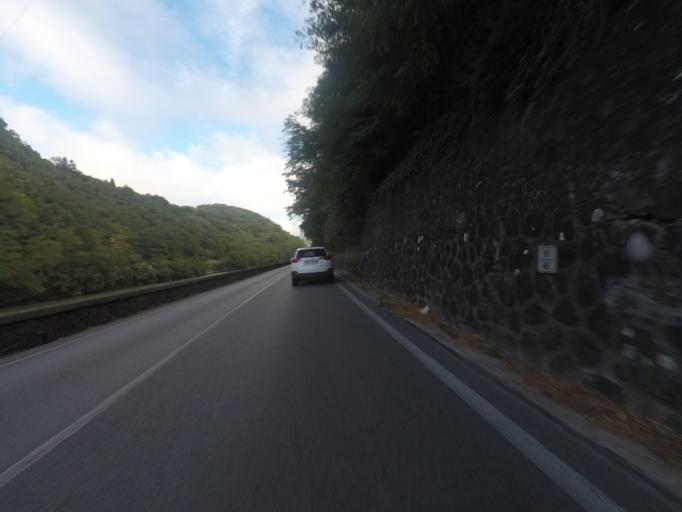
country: IT
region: Tuscany
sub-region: Provincia di Lucca
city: Borgo a Mozzano
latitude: 43.9877
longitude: 10.5530
